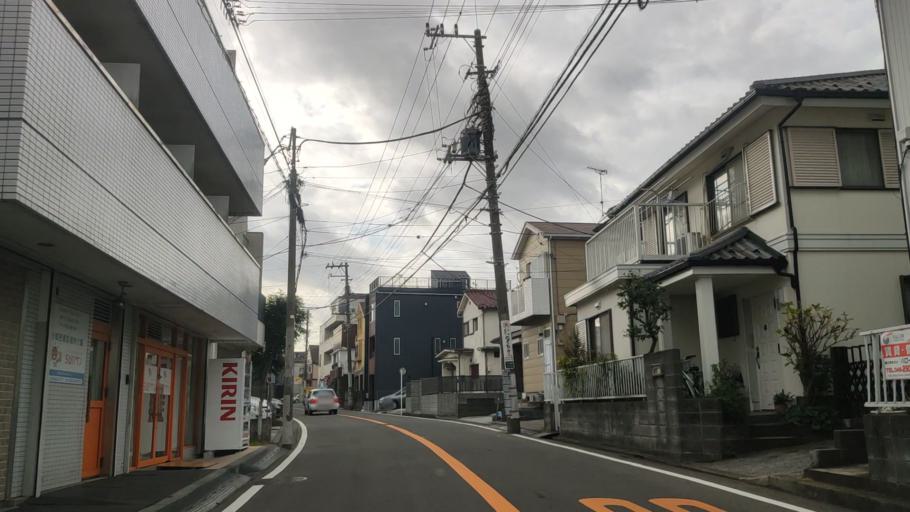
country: JP
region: Kanagawa
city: Yokohama
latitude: 35.4855
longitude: 139.6229
